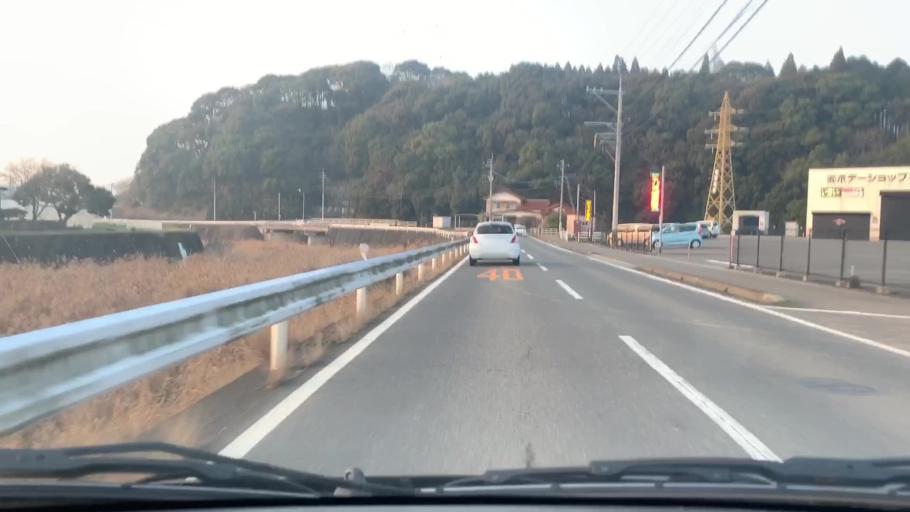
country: JP
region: Saga Prefecture
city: Imaricho-ko
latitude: 33.2708
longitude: 129.8952
